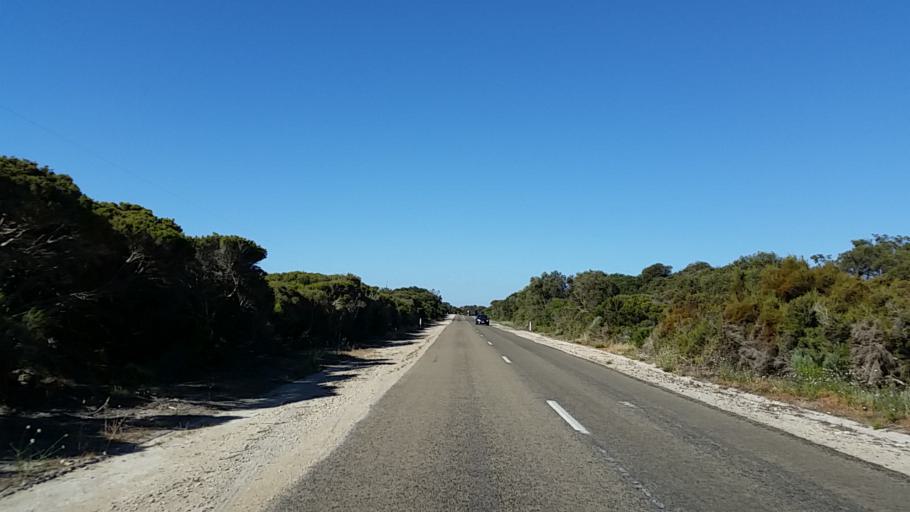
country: AU
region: South Australia
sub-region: Yorke Peninsula
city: Honiton
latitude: -35.2505
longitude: 136.9672
